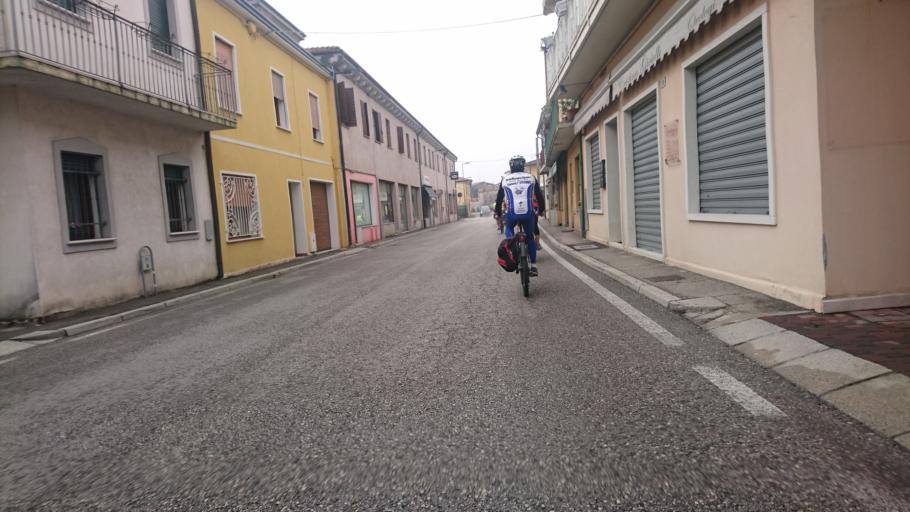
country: IT
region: Veneto
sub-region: Provincia di Padova
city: Pozzonovo
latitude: 45.1964
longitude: 11.7926
